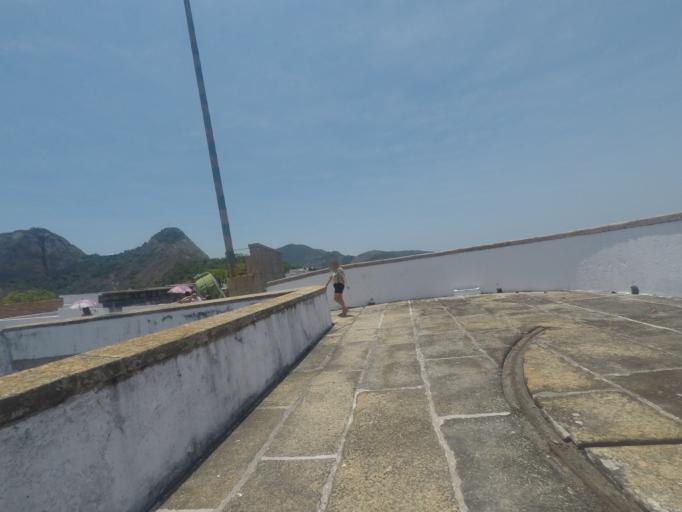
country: BR
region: Rio de Janeiro
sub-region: Niteroi
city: Niteroi
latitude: -22.9383
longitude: -43.1345
